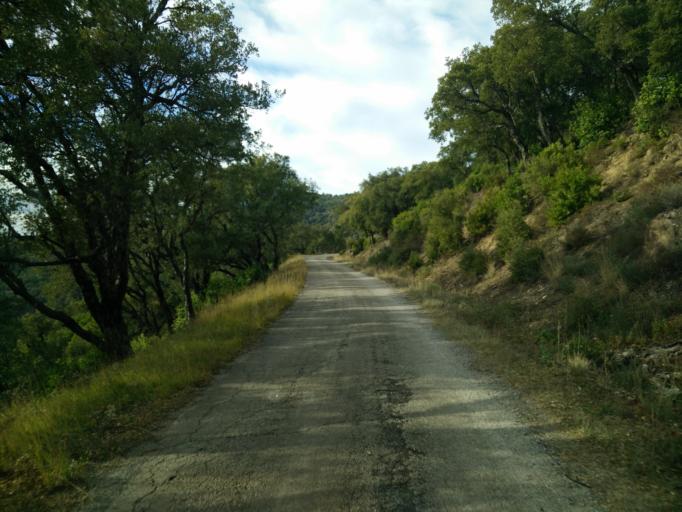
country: FR
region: Provence-Alpes-Cote d'Azur
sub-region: Departement du Var
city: Roquebrune-sur-Argens
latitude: 43.3984
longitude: 6.6309
